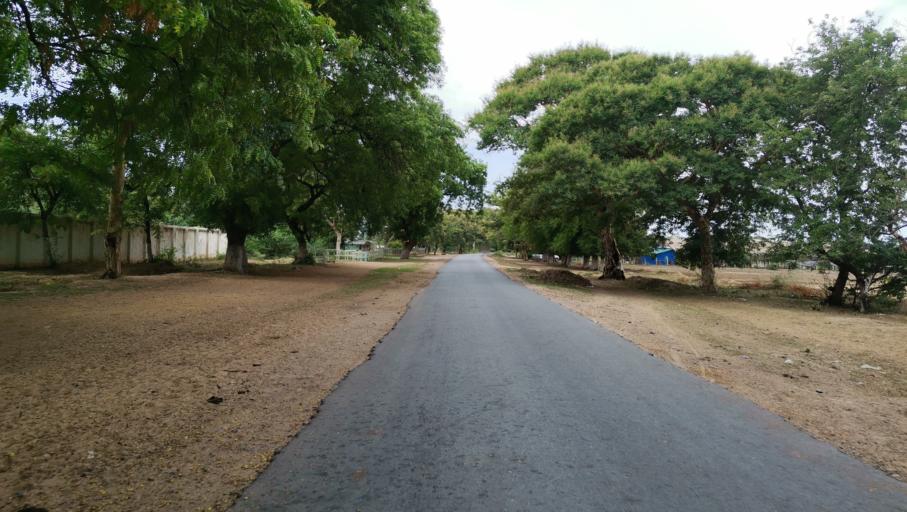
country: MM
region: Mandalay
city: Myingyan
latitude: 21.8485
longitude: 95.4300
